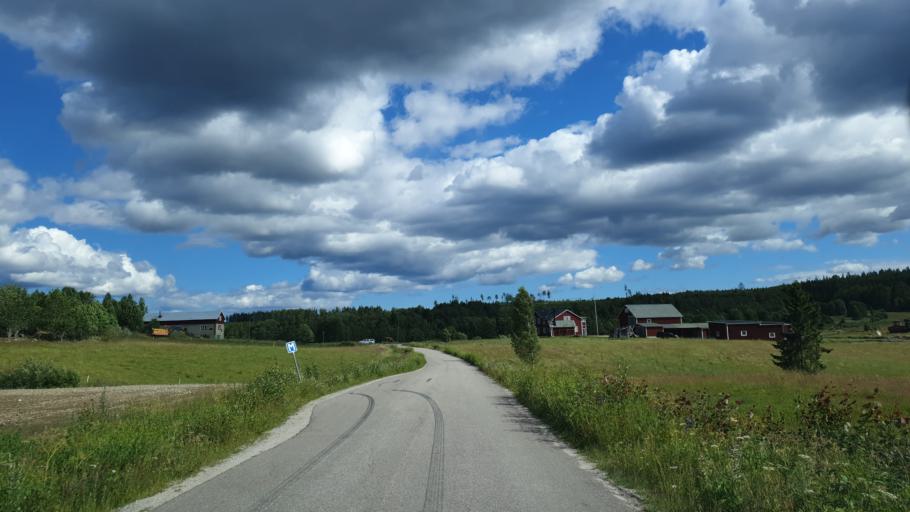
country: SE
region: Gaevleborg
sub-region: Nordanstigs Kommun
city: Bergsjoe
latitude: 62.0381
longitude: 17.0990
